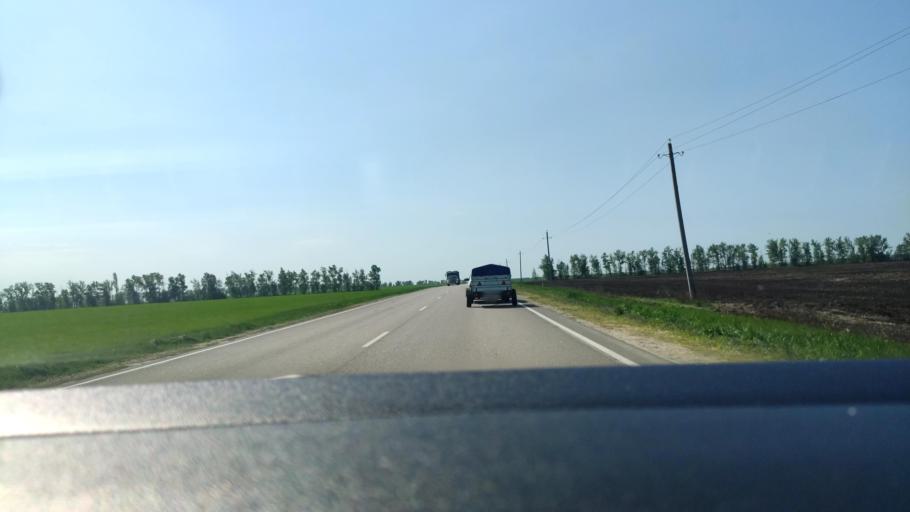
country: RU
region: Voronezj
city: Novaya Usman'
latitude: 51.5689
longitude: 39.3762
